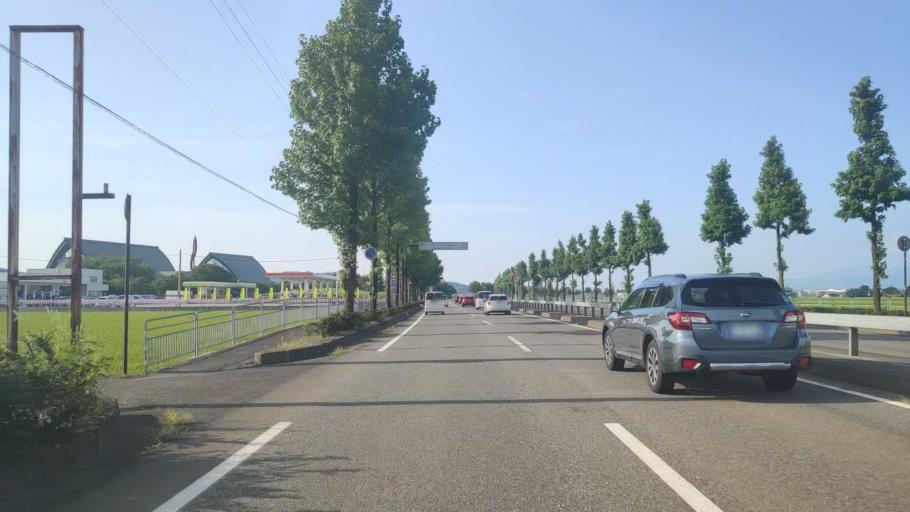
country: JP
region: Fukui
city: Fukui-shi
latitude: 36.0110
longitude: 136.2092
